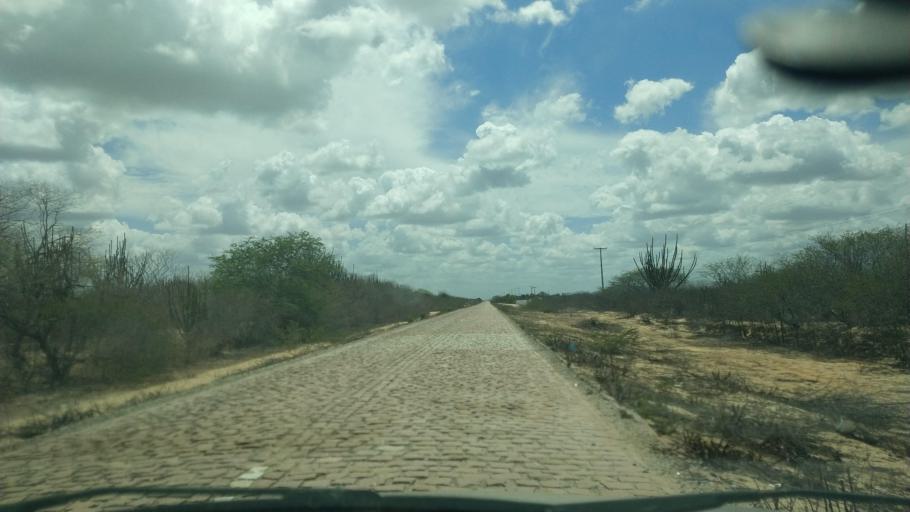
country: BR
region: Rio Grande do Norte
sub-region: Sao Paulo Do Potengi
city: Sao Paulo do Potengi
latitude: -5.9680
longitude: -35.8522
